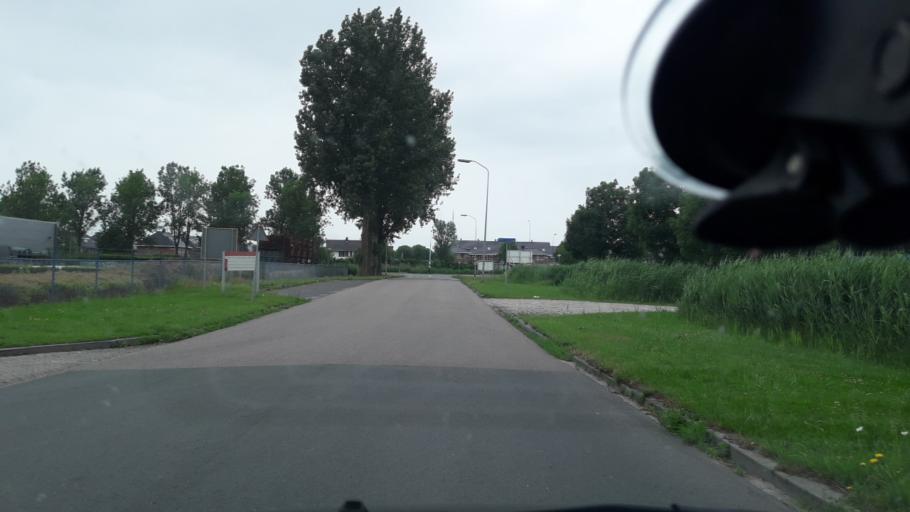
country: NL
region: Flevoland
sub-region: Gemeente Lelystad
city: Lelystad
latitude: 52.5047
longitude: 5.4393
